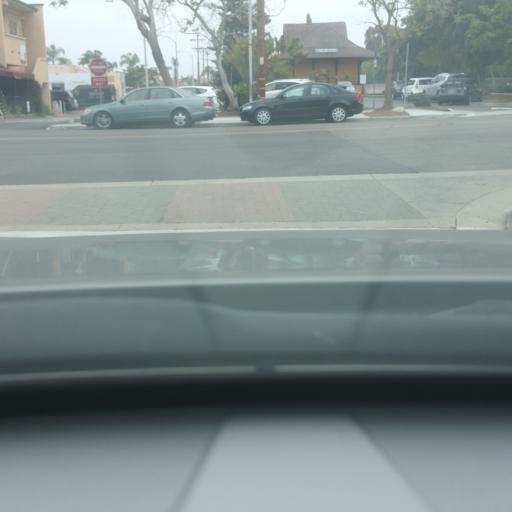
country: US
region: California
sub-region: San Diego County
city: Carlsbad
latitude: 33.1606
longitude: -117.3502
